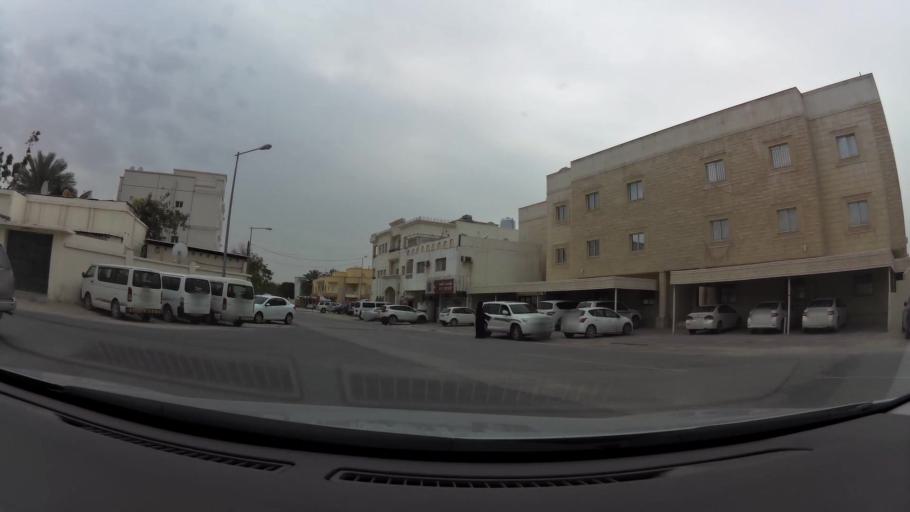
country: QA
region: Baladiyat ad Dawhah
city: Doha
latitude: 25.3136
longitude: 51.4933
